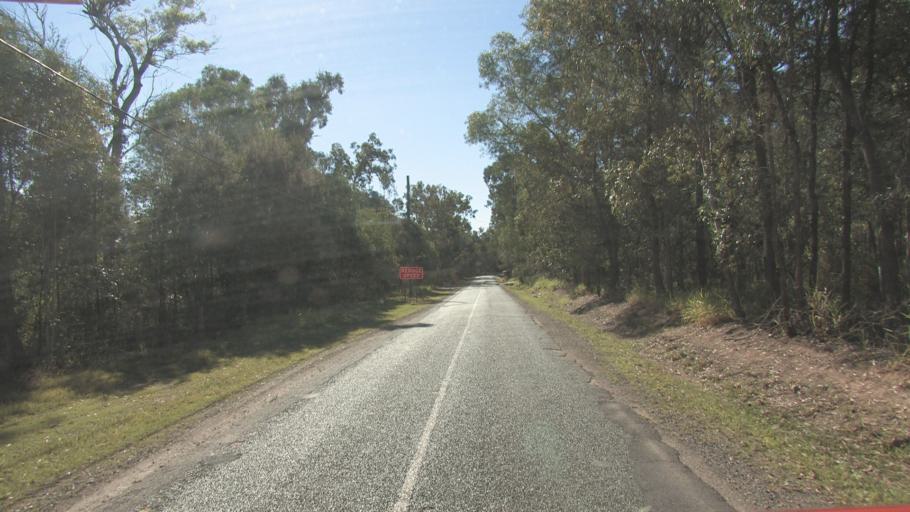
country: AU
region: Queensland
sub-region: Logan
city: Chambers Flat
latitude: -27.7947
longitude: 153.0703
